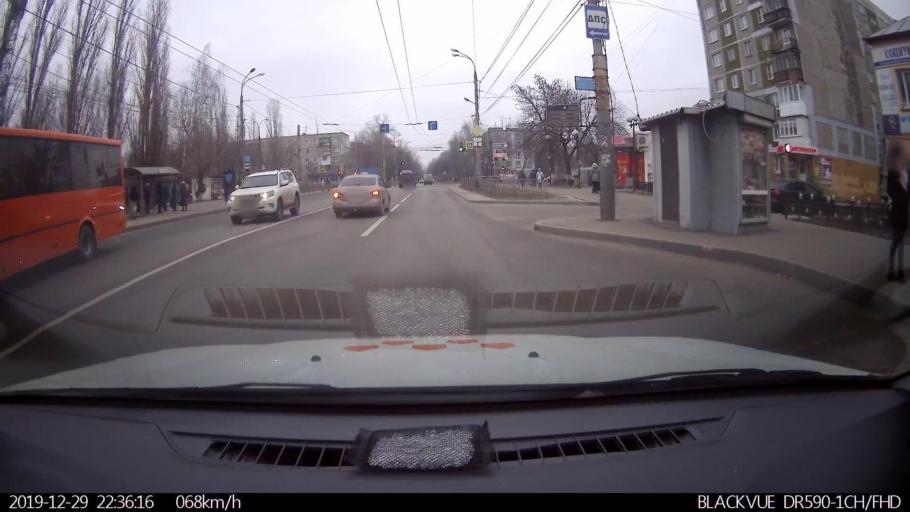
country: RU
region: Nizjnij Novgorod
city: Nizhniy Novgorod
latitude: 56.2662
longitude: 43.8909
